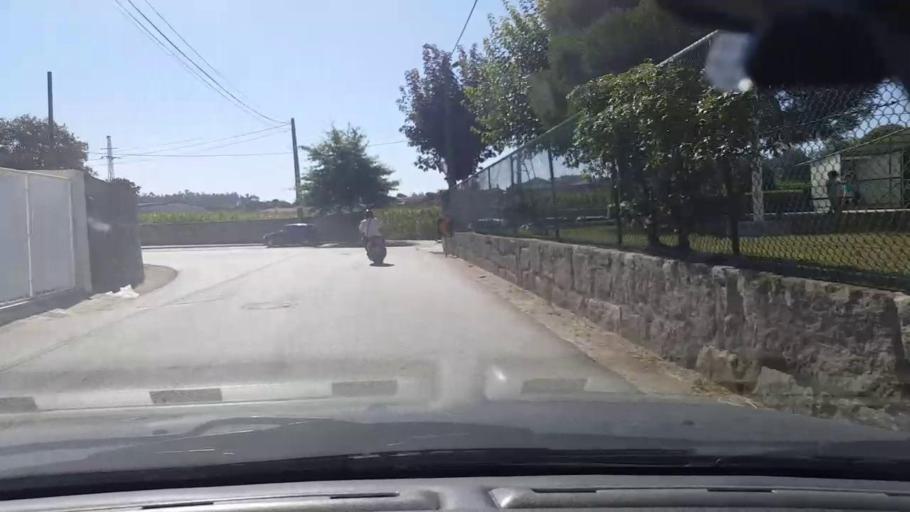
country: PT
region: Porto
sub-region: Matosinhos
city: Lavra
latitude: 41.2689
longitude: -8.6912
